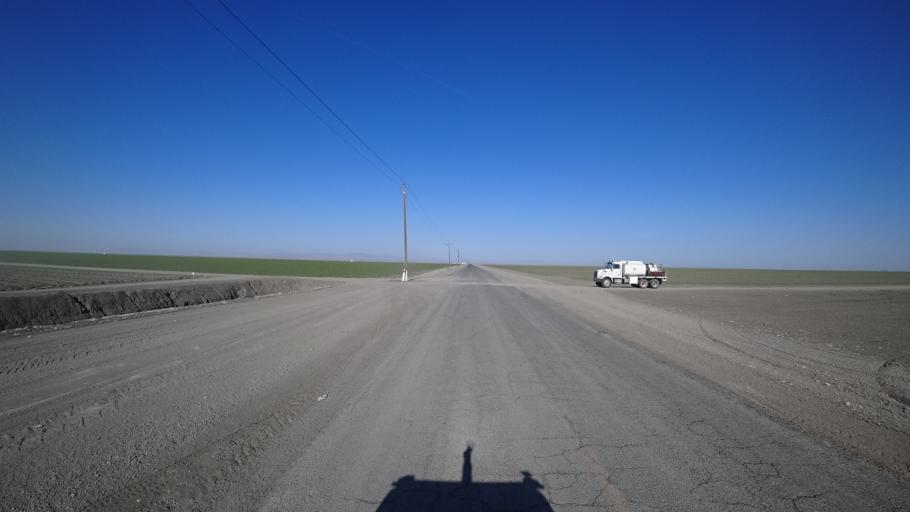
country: US
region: California
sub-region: Kings County
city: Stratford
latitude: 36.0797
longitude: -119.7706
